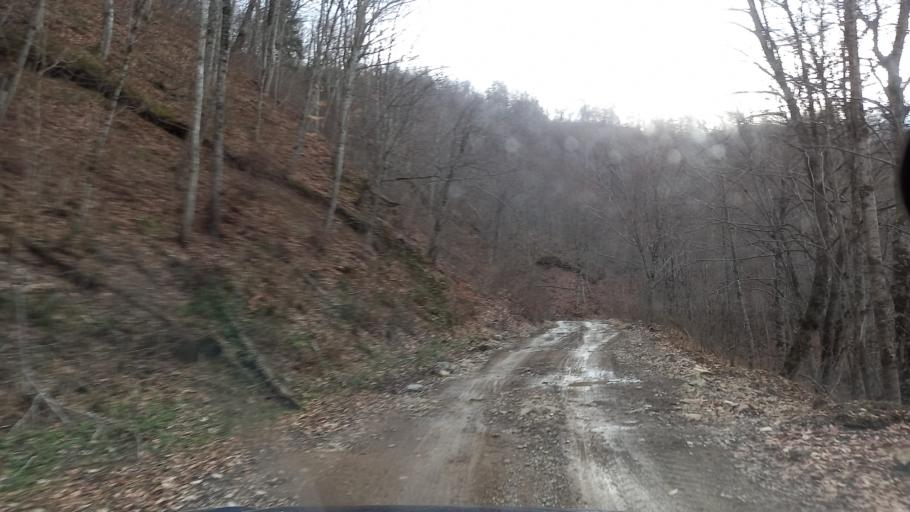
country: RU
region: Adygeya
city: Kamennomostskiy
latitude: 44.1549
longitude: 40.3028
